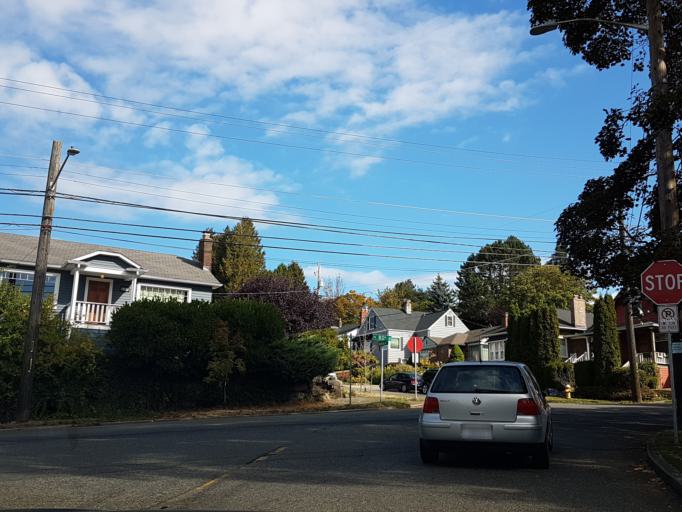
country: US
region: Washington
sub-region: King County
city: Shoreline
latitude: 47.6868
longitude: -122.3348
